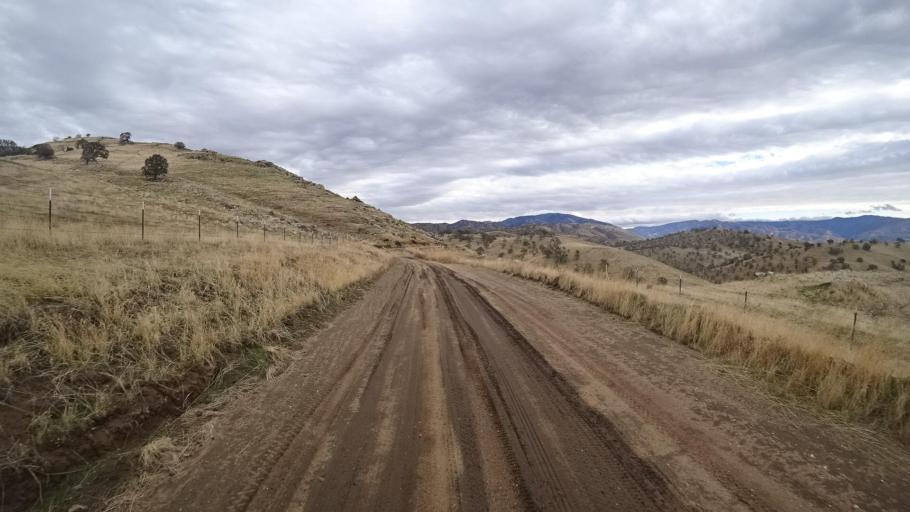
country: US
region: California
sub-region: Kern County
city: Stallion Springs
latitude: 35.1246
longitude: -118.7508
